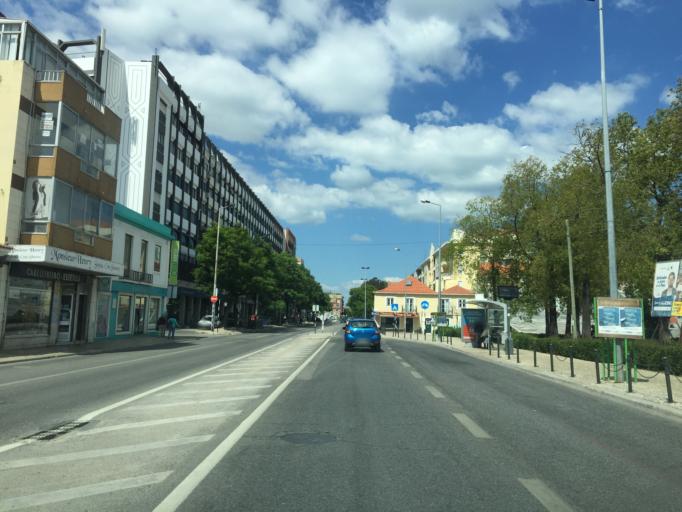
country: PT
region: Setubal
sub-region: Almada
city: Almada
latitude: 38.6705
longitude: -9.1577
